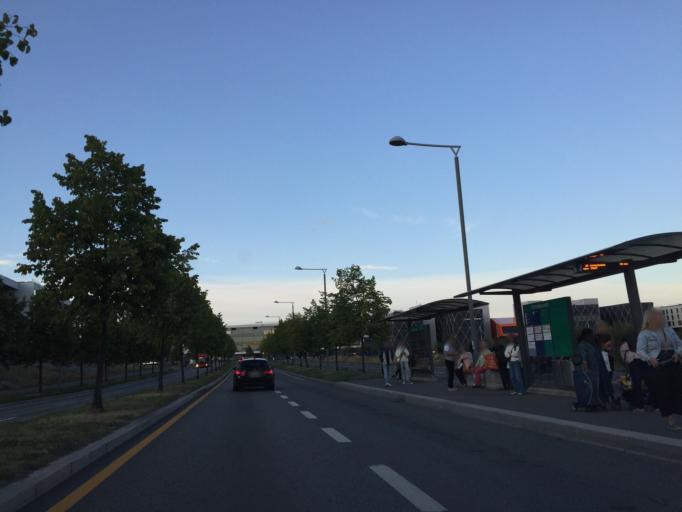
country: NO
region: Akershus
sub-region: Baerum
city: Lysaker
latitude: 59.8936
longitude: 10.6224
